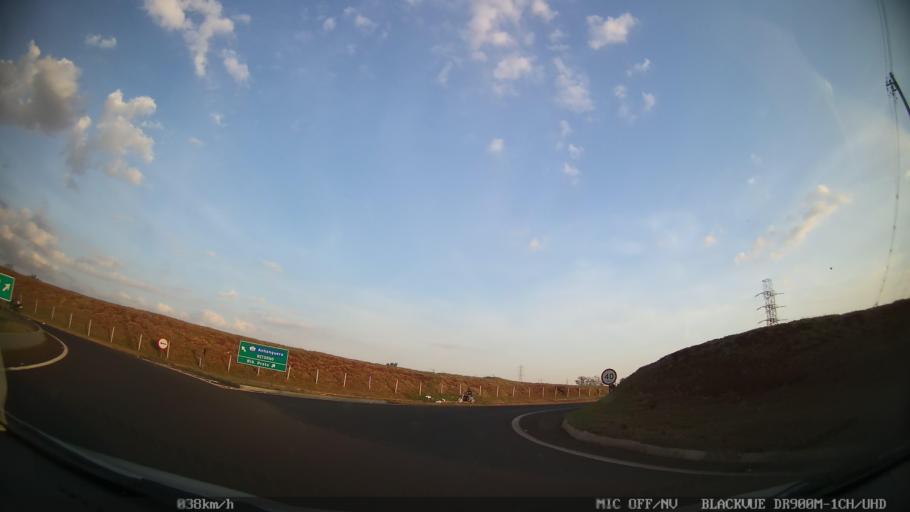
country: BR
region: Sao Paulo
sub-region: Ribeirao Preto
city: Ribeirao Preto
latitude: -21.1345
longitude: -47.8569
